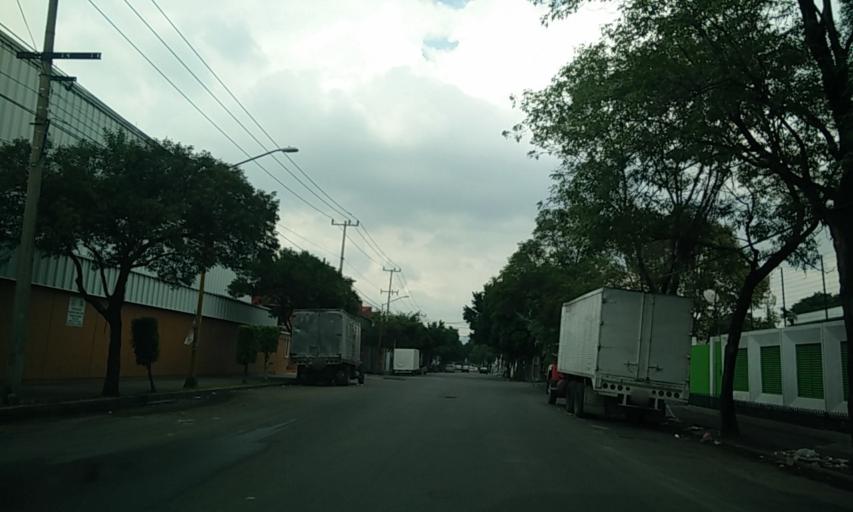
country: MX
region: Mexico City
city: Azcapotzalco
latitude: 19.4815
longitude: -99.1572
